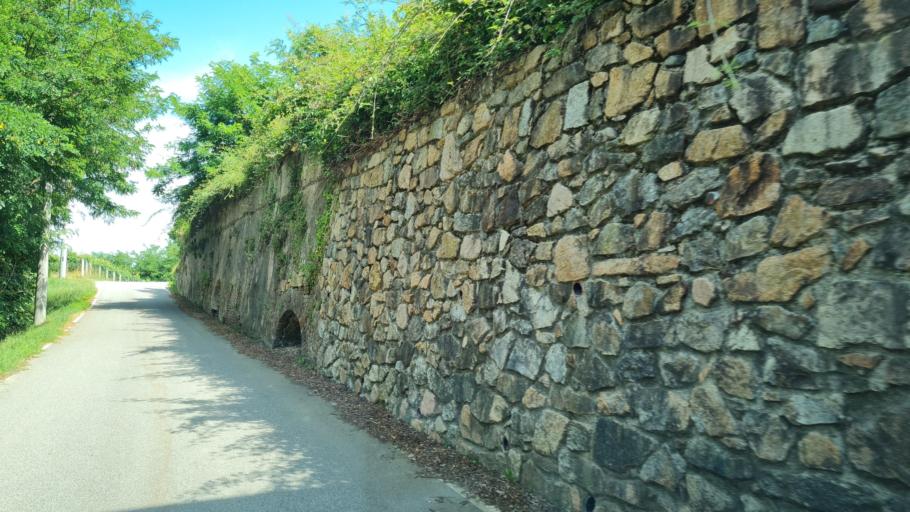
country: IT
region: Piedmont
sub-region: Provincia di Biella
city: Masserano
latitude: 45.5792
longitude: 8.2125
